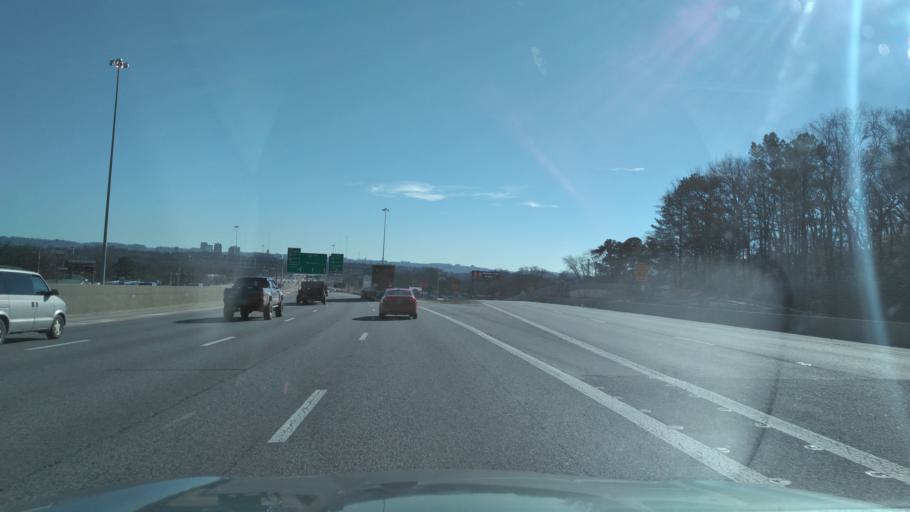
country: US
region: Alabama
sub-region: Jefferson County
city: Birmingham
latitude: 33.5545
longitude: -86.8314
